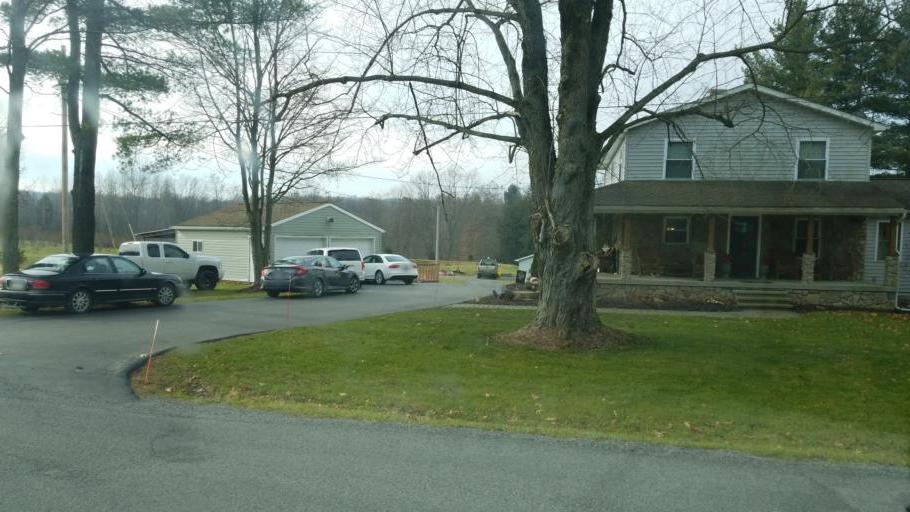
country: US
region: Pennsylvania
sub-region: Crawford County
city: Cochranton
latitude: 41.5202
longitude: -80.1232
